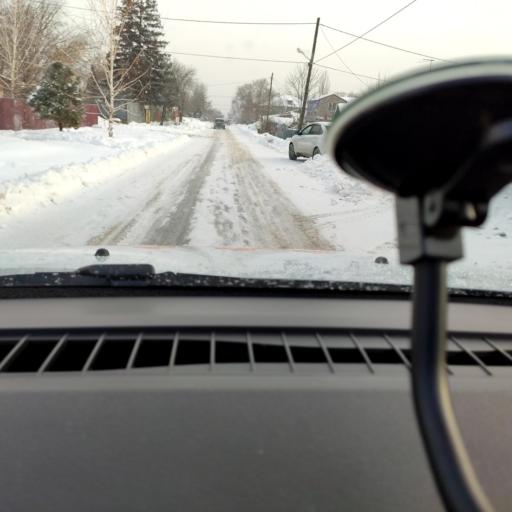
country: RU
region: Samara
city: Samara
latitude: 53.2044
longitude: 50.2061
